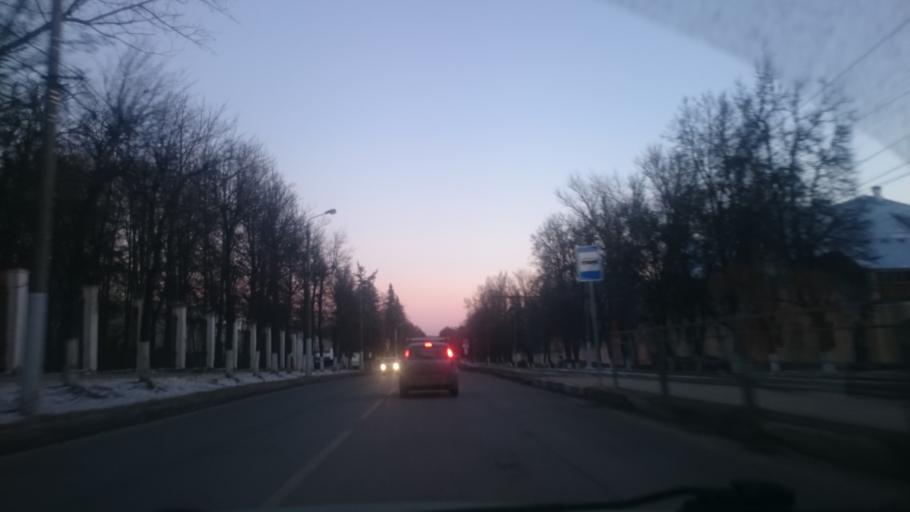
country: RU
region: Tula
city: Tula
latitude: 54.1850
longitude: 37.6982
